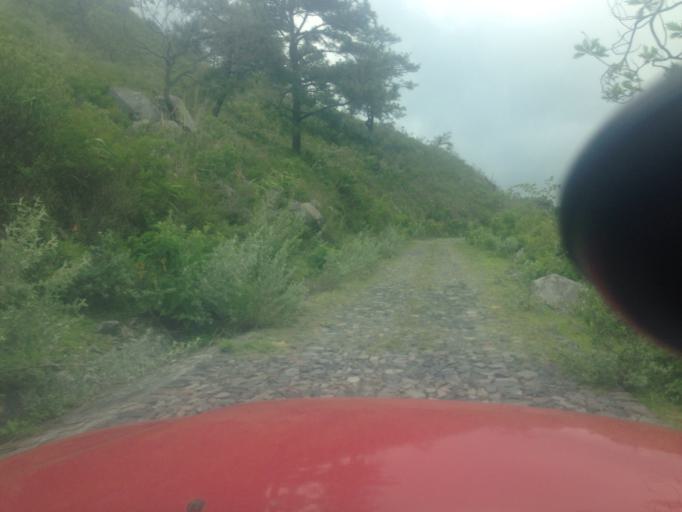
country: MX
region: Nayarit
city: Jala
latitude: 21.1251
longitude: -104.4998
